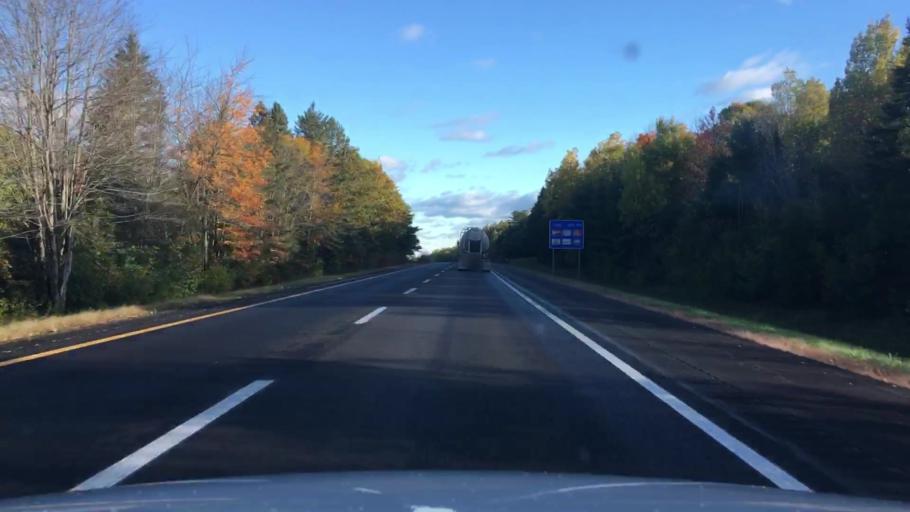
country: US
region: Maine
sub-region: Penobscot County
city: Orono
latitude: 44.8908
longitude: -68.6924
